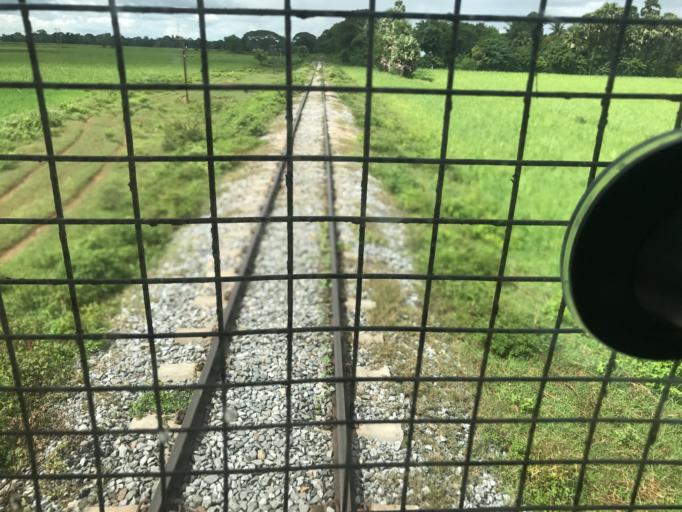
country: MM
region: Bago
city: Paungde
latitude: 18.6778
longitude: 95.4040
